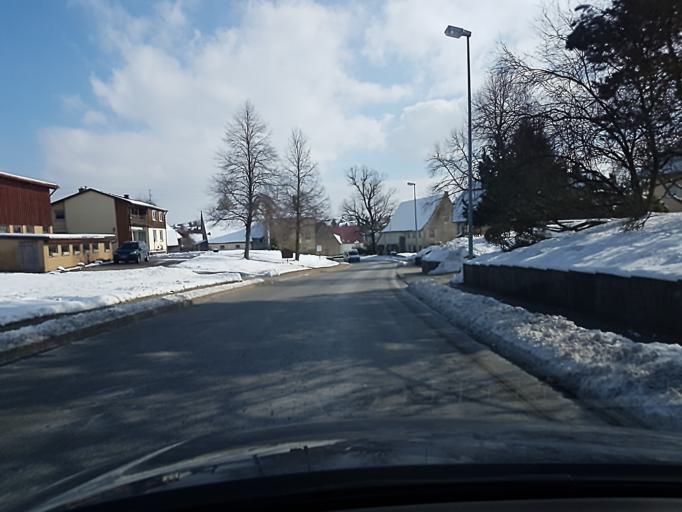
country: DE
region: Baden-Wuerttemberg
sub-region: Freiburg Region
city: Oberndorf
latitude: 48.3240
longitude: 8.5596
